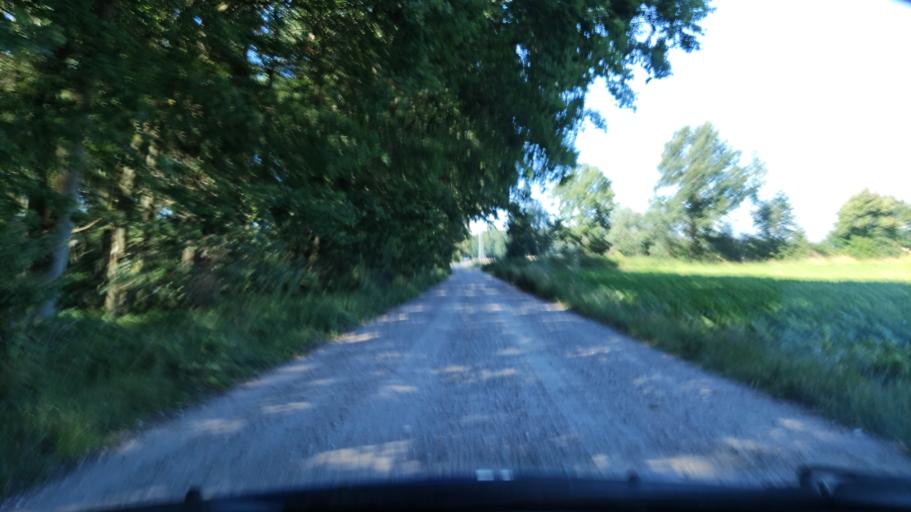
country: DE
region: Lower Saxony
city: Thomasburg
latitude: 53.1856
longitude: 10.6756
